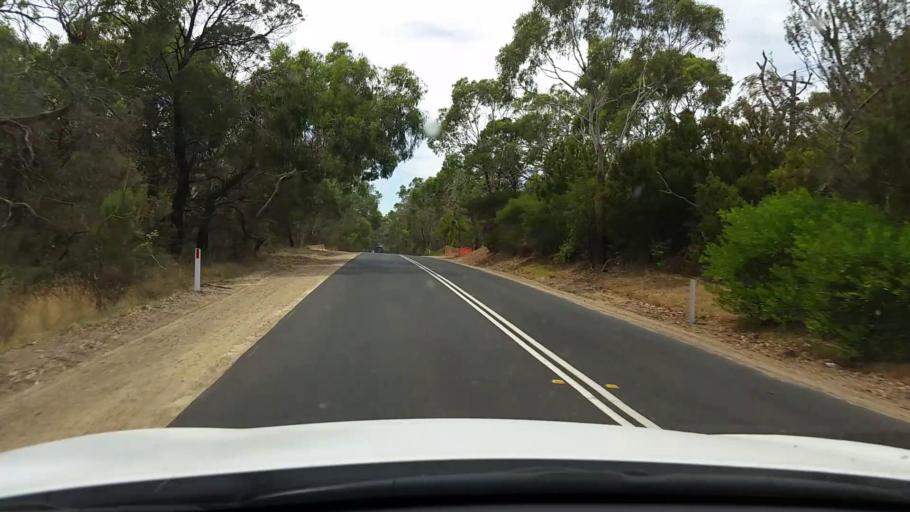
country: AU
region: Victoria
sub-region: Mornington Peninsula
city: Mount Martha
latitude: -38.3020
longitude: 145.0419
